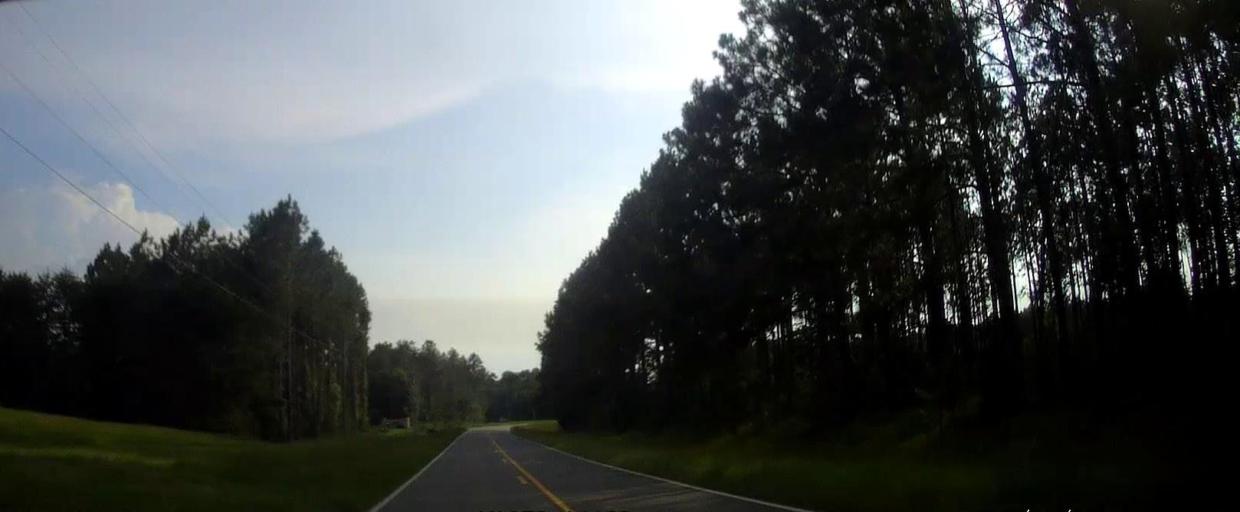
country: US
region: Georgia
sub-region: Laurens County
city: Dublin
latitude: 32.4808
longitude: -82.9506
